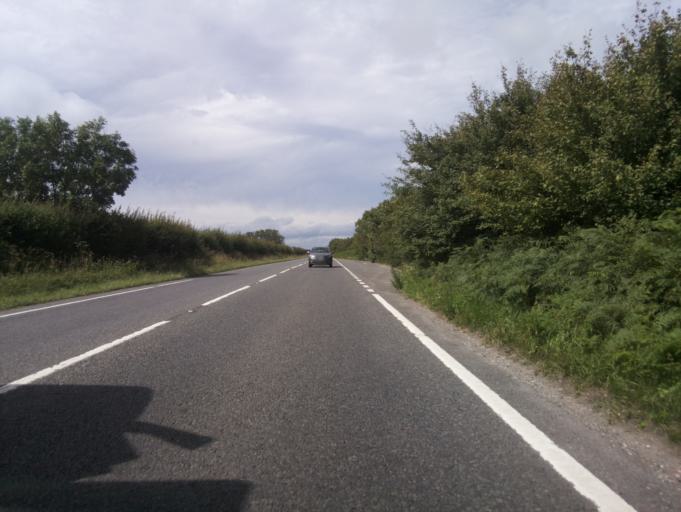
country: GB
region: England
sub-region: Dorset
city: Sherborne
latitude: 50.8054
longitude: -2.5519
